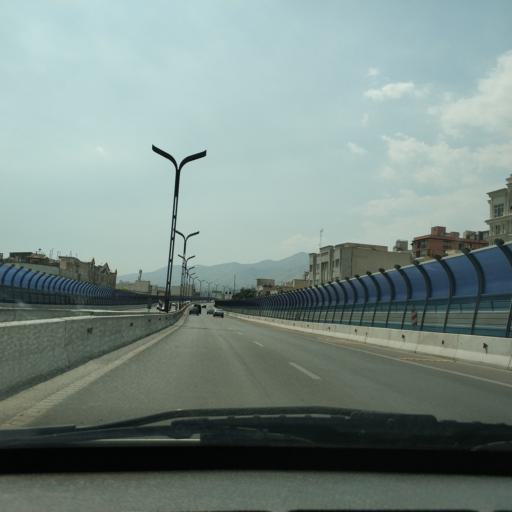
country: IR
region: Tehran
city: Tajrish
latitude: 35.7915
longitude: 51.4691
